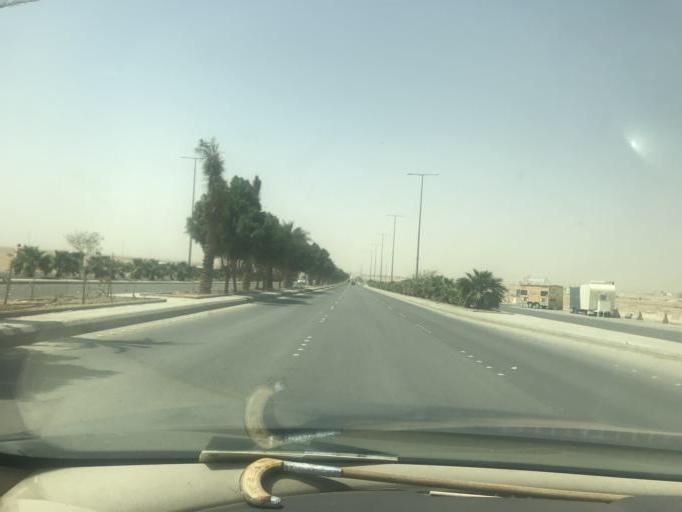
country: SA
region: Ar Riyad
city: Riyadh
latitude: 24.8018
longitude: 46.5832
